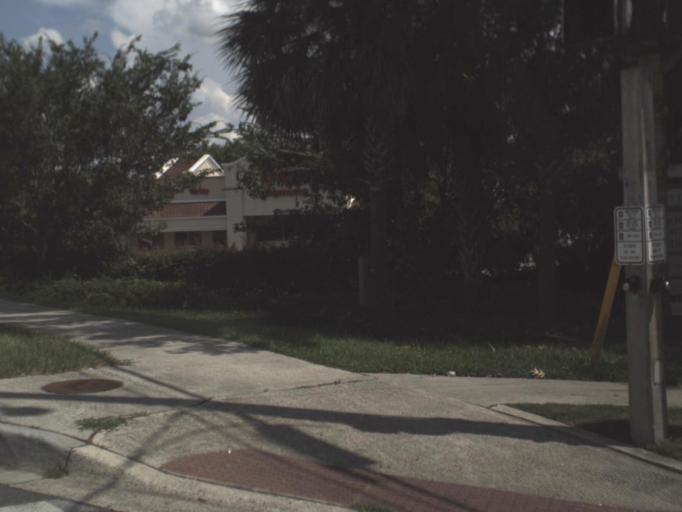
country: US
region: Florida
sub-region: Alachua County
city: Alachua
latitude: 29.7944
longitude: -82.4956
